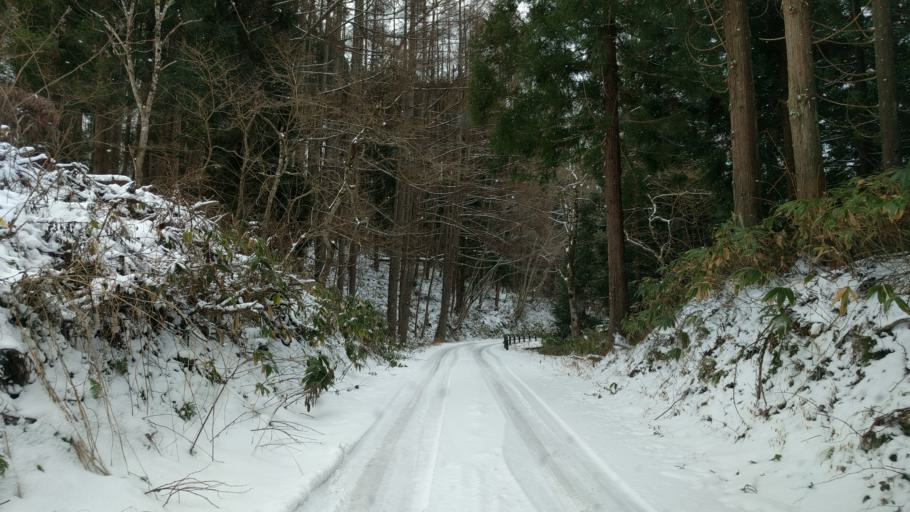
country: JP
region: Fukushima
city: Inawashiro
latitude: 37.3876
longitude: 140.0222
